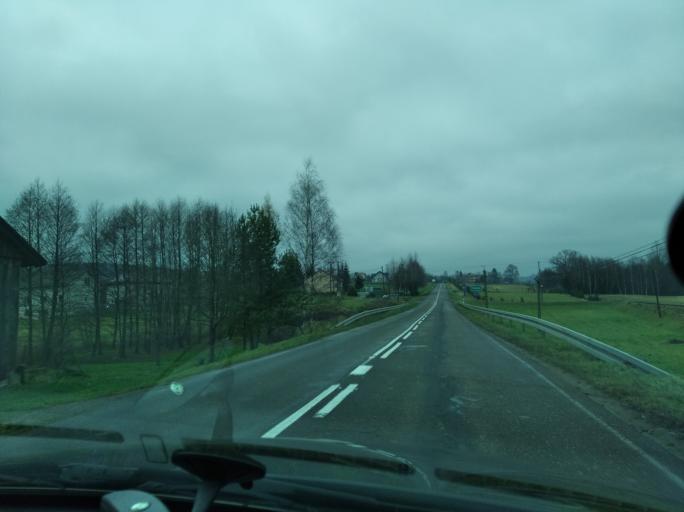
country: PL
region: Subcarpathian Voivodeship
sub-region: Powiat rzeszowski
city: Dynow
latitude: 49.8582
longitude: 22.2496
